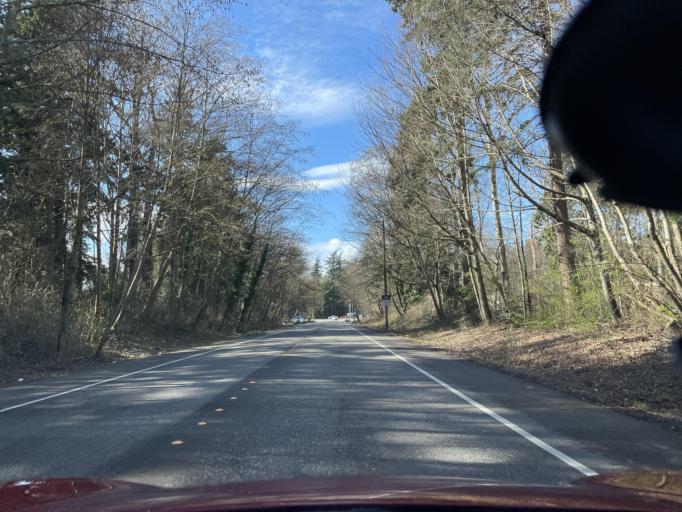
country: US
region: Washington
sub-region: Whatcom County
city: Bellingham
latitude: 48.7772
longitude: -122.4824
